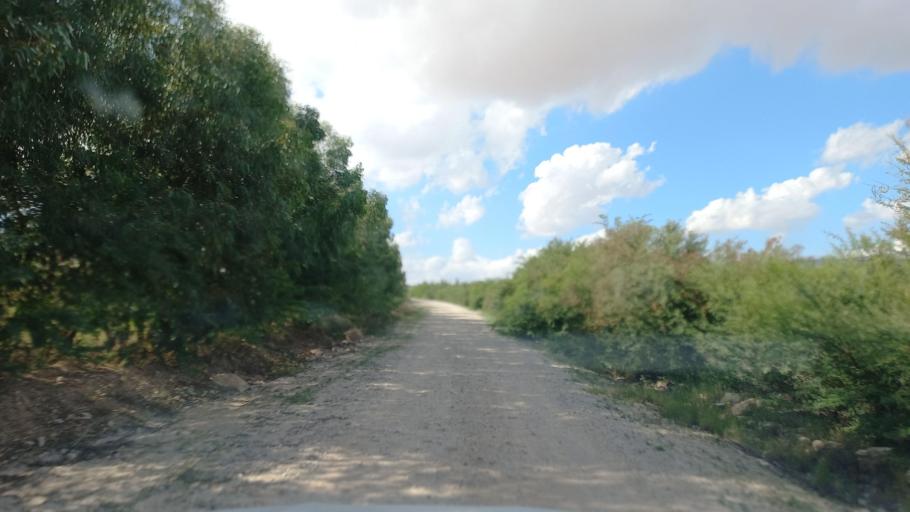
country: TN
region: Al Qasrayn
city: Sbiba
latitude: 35.3383
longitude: 9.0782
